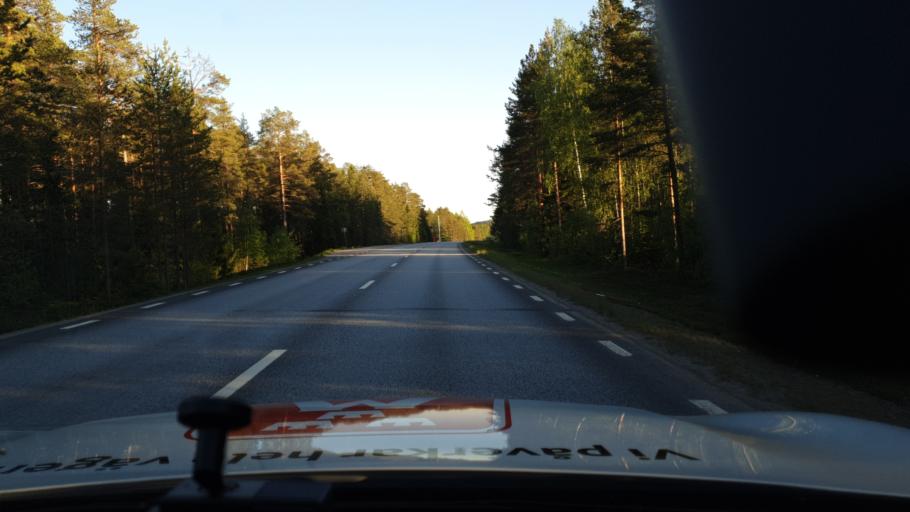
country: SE
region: Vaesterbotten
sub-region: Umea Kommun
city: Ersmark
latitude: 63.8960
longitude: 20.3140
